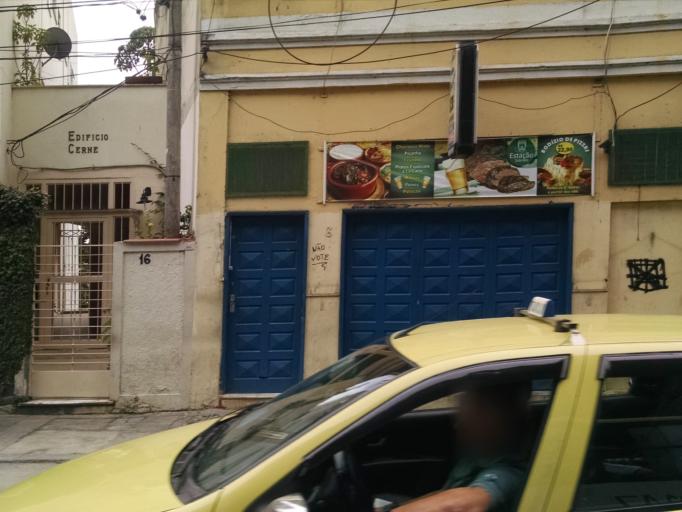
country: BR
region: Rio de Janeiro
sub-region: Rio De Janeiro
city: Rio de Janeiro
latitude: -22.9199
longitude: -43.1845
